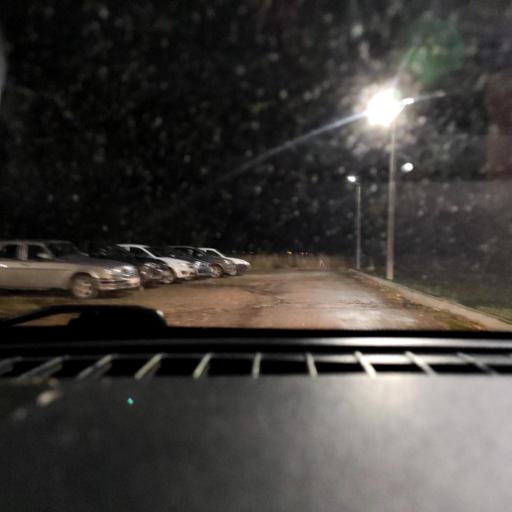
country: RU
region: Perm
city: Froly
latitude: 57.9553
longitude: 56.2753
